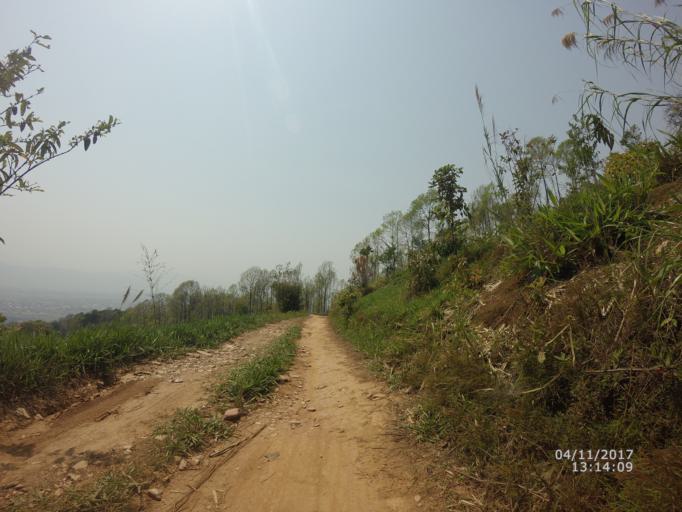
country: NP
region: Western Region
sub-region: Gandaki Zone
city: Pokhara
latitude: 28.2099
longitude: 84.0388
